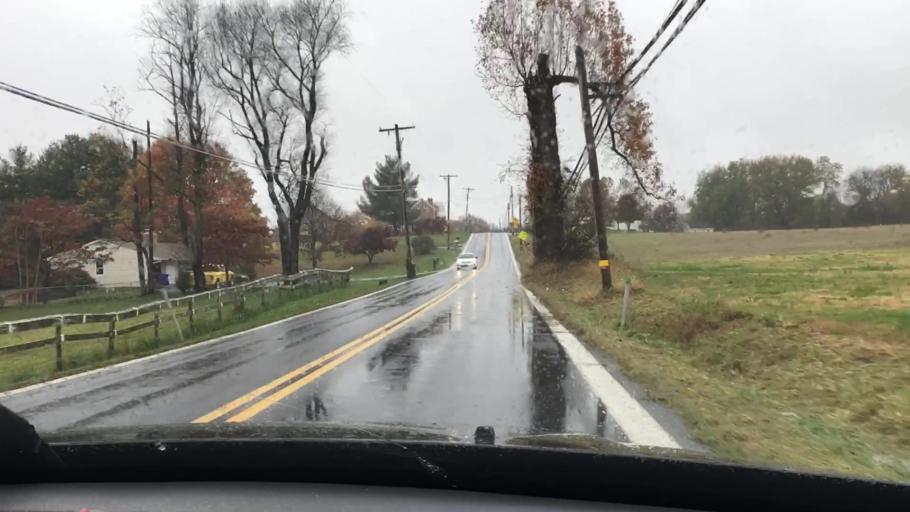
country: US
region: Maryland
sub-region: Frederick County
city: Urbana
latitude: 39.3327
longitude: -77.3899
